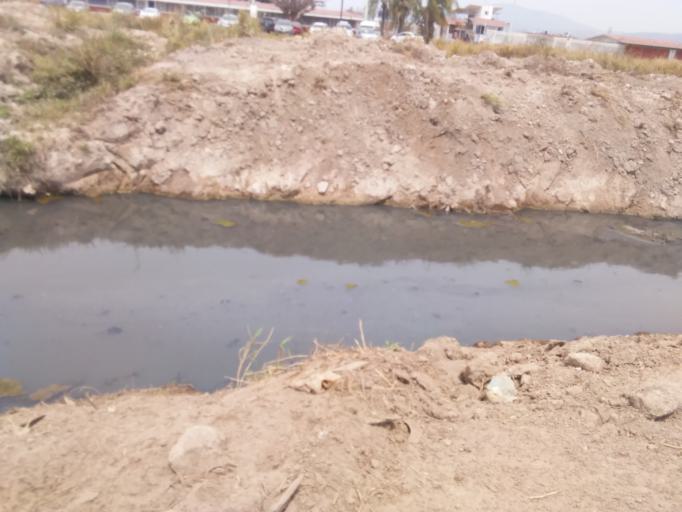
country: MX
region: Nayarit
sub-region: Tepic
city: La Corregidora
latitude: 21.4810
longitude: -104.8427
